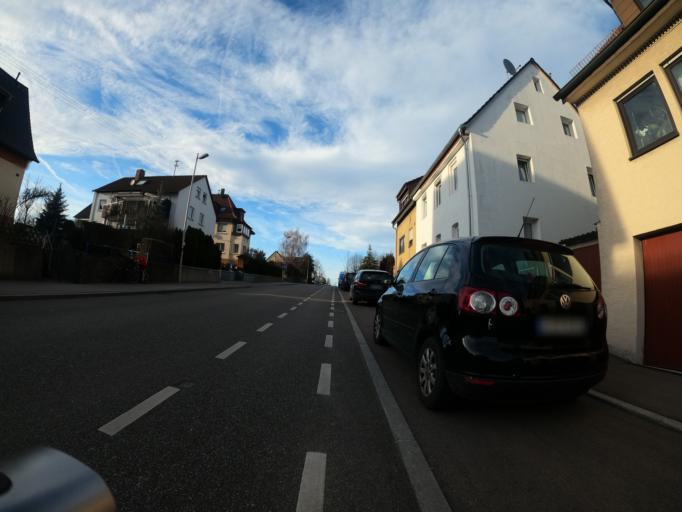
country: DE
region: Baden-Wuerttemberg
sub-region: Regierungsbezirk Stuttgart
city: Denkendorf
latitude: 48.6990
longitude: 9.3119
